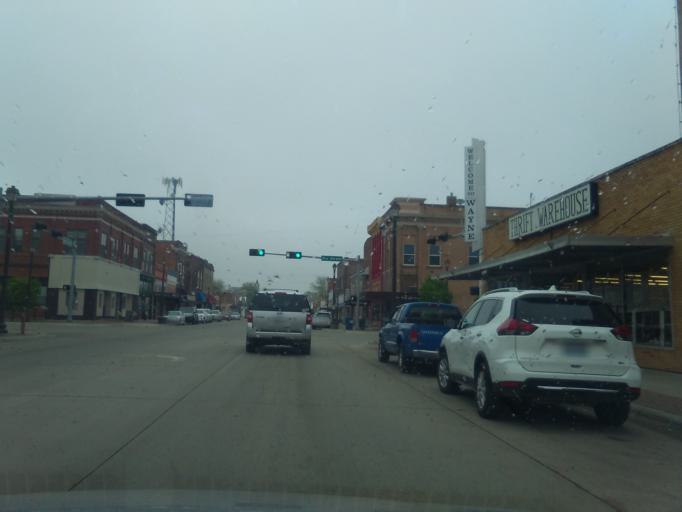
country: US
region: Nebraska
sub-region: Wayne County
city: Wayne
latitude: 42.2299
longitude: -97.0178
